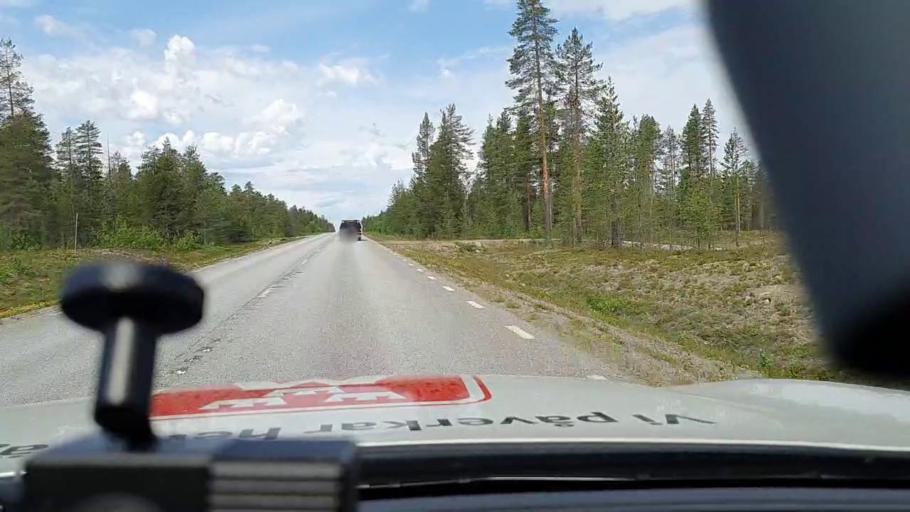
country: SE
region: Norrbotten
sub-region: Jokkmokks Kommun
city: Jokkmokk
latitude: 66.5242
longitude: 20.2015
